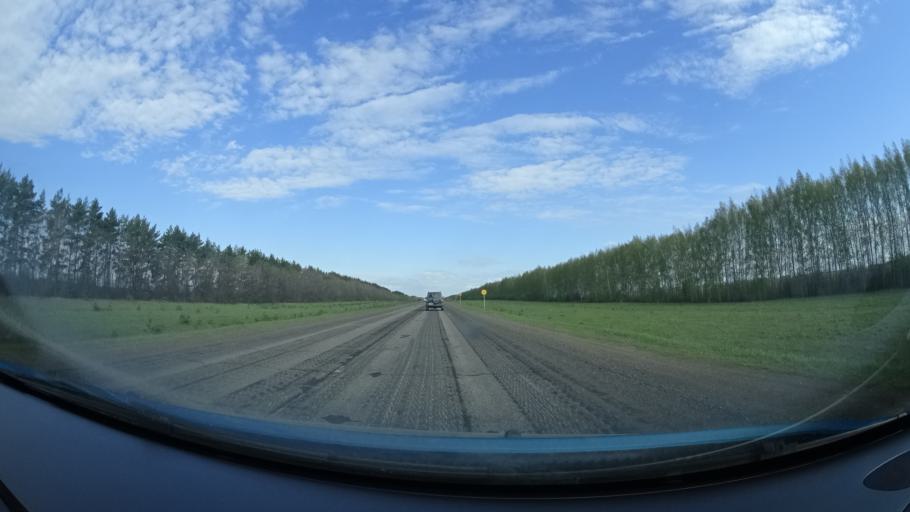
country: RU
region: Bashkortostan
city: Blagoveshchensk
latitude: 55.2195
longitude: 55.7996
